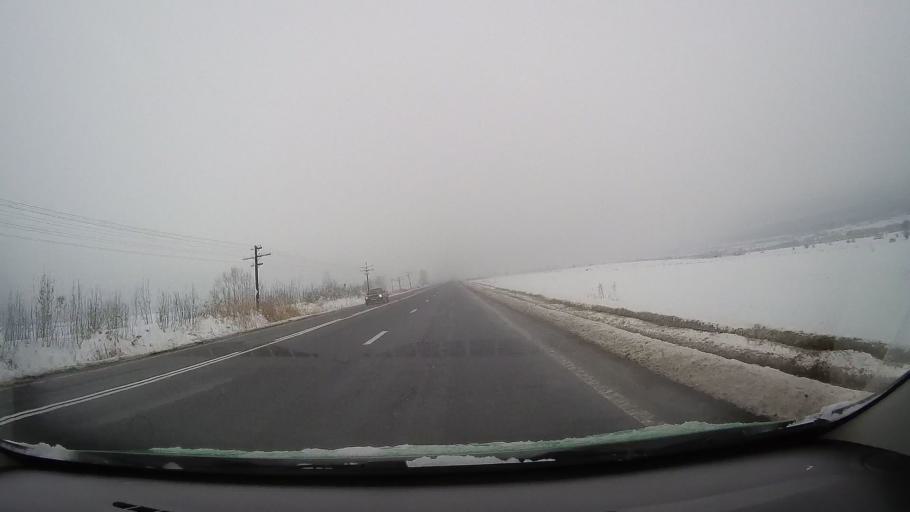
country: RO
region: Sibiu
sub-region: Oras Saliste
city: Saliste
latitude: 45.7943
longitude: 23.9143
